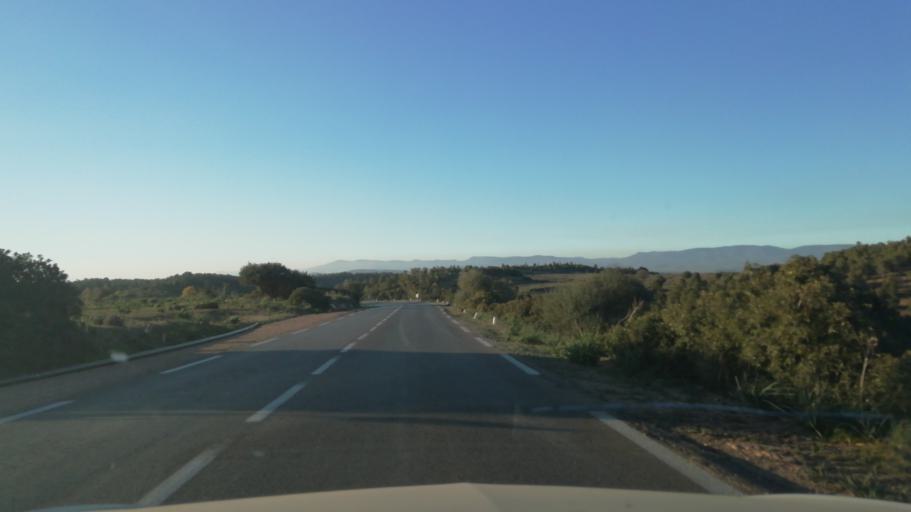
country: DZ
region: Tlemcen
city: Beni Mester
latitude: 34.8133
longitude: -1.6264
